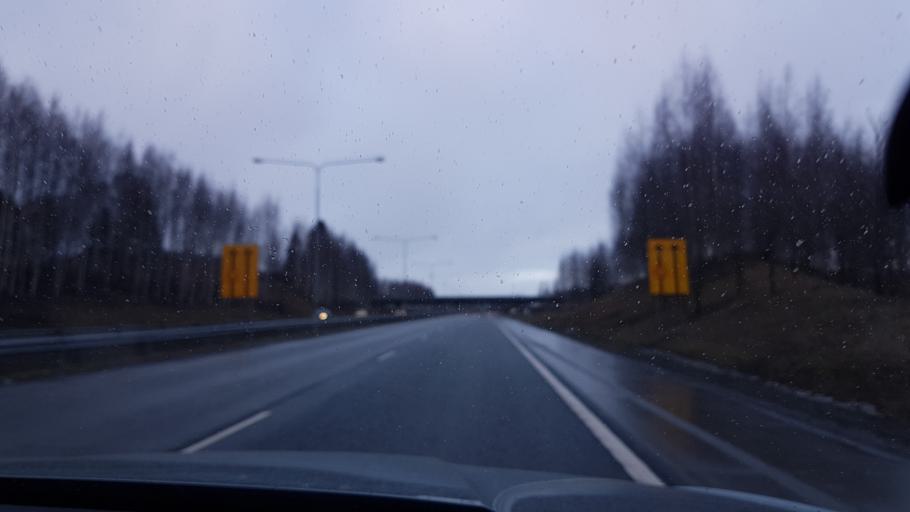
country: FI
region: Pirkanmaa
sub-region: Tampere
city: Tampere
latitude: 61.4858
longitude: 23.8741
